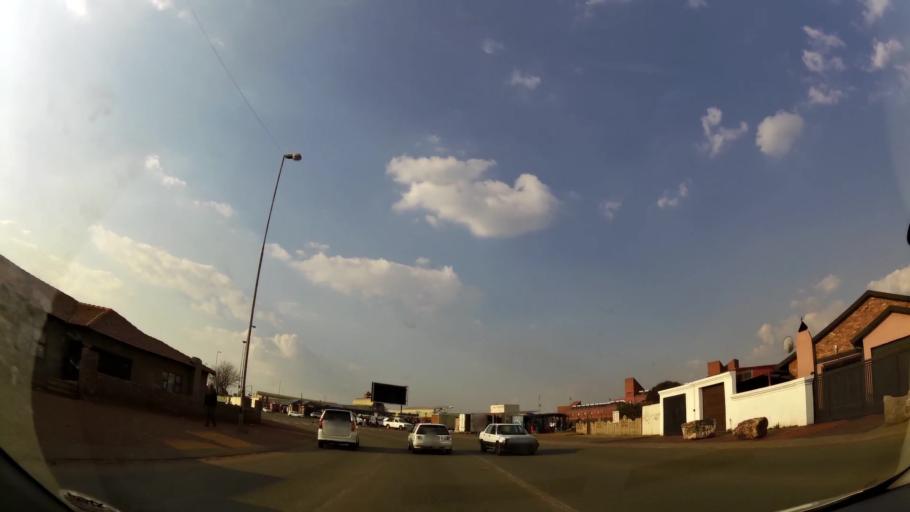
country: ZA
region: Gauteng
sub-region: Ekurhuleni Metropolitan Municipality
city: Germiston
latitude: -26.3547
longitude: 28.1966
